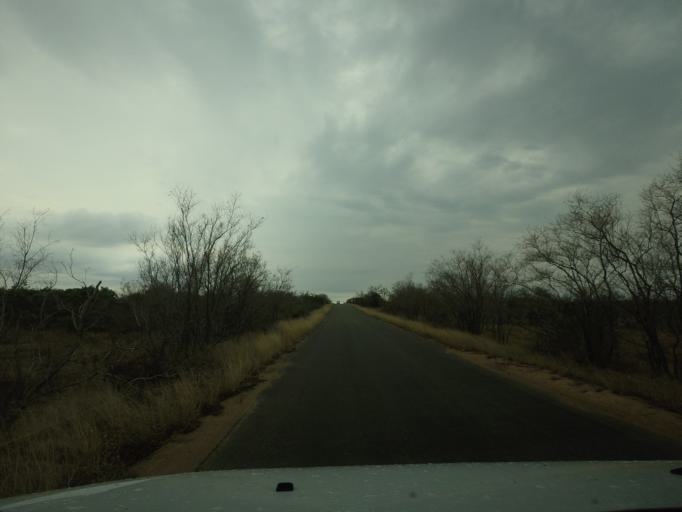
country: ZA
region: Limpopo
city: Thulamahashi
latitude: -24.4686
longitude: 31.4432
